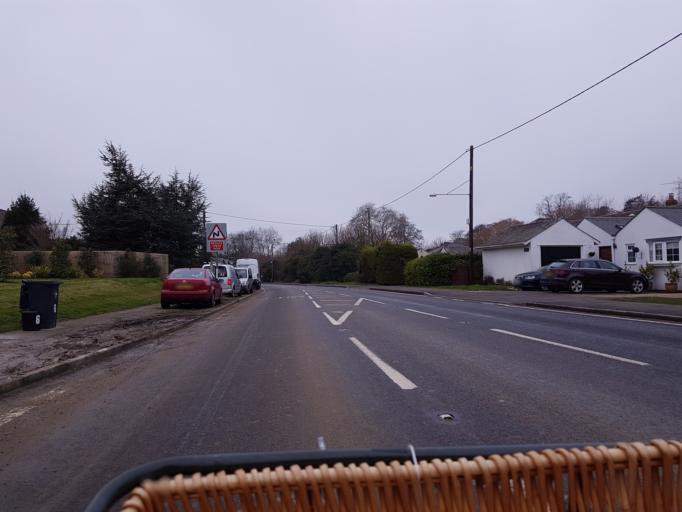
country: GB
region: England
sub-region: Cambridgeshire
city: Duxford
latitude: 52.0603
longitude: 0.1955
